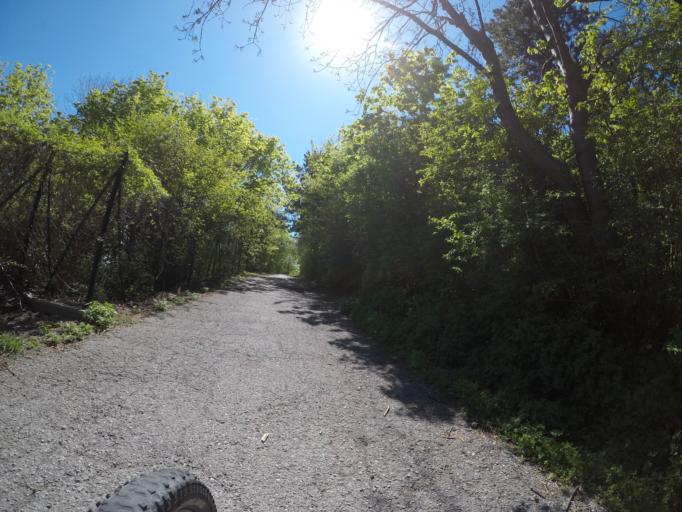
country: AT
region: Lower Austria
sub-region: Politischer Bezirk Modling
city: Modling
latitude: 48.0791
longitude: 16.2797
